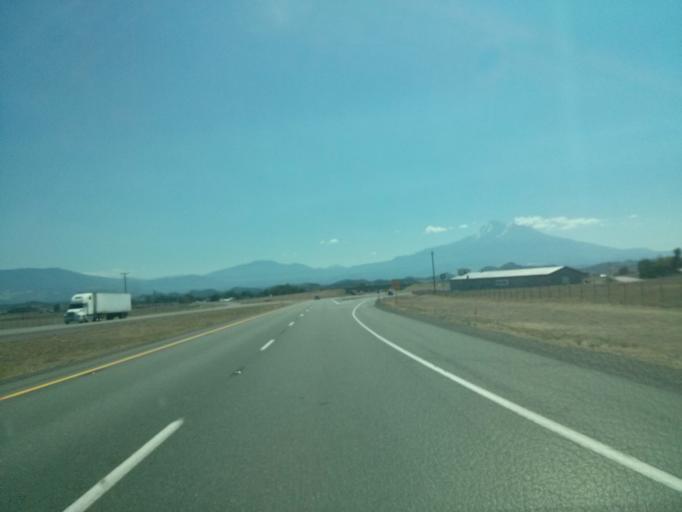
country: US
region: California
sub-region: Siskiyou County
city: Montague
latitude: 41.6489
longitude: -122.5412
